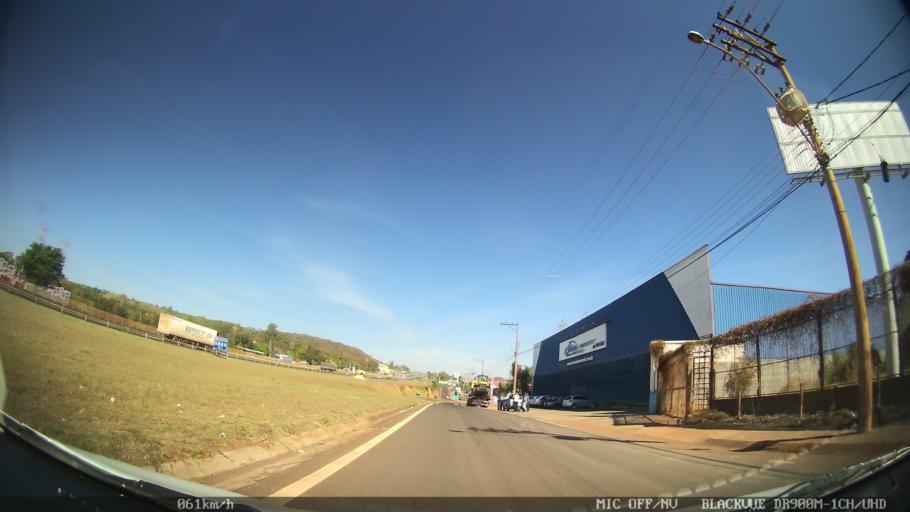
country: BR
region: Sao Paulo
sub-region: Ribeirao Preto
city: Ribeirao Preto
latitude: -21.2216
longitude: -47.7596
